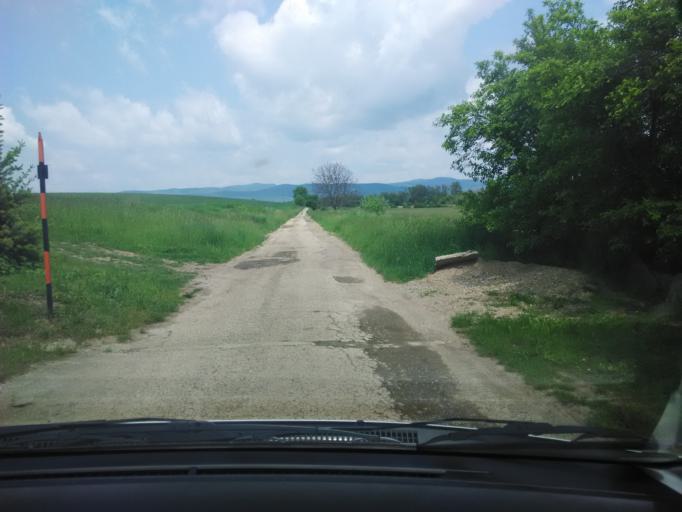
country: SK
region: Nitriansky
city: Levice
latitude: 48.2648
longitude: 18.7042
